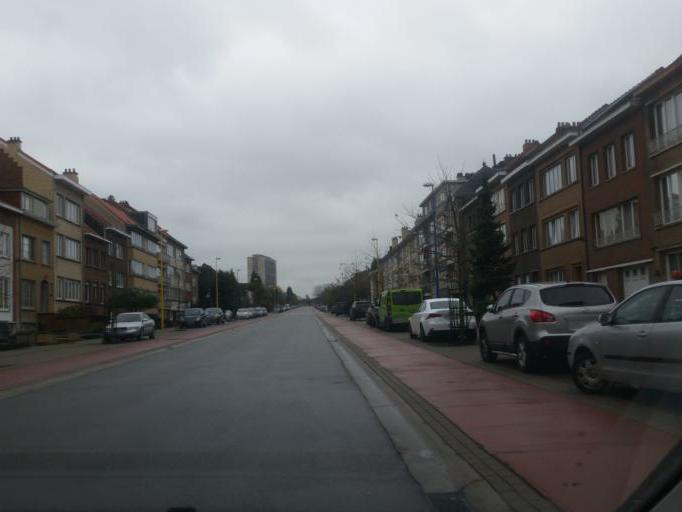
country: BE
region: Flanders
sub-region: Provincie Vlaams-Brabant
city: Grimbergen
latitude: 50.9081
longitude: 4.3564
